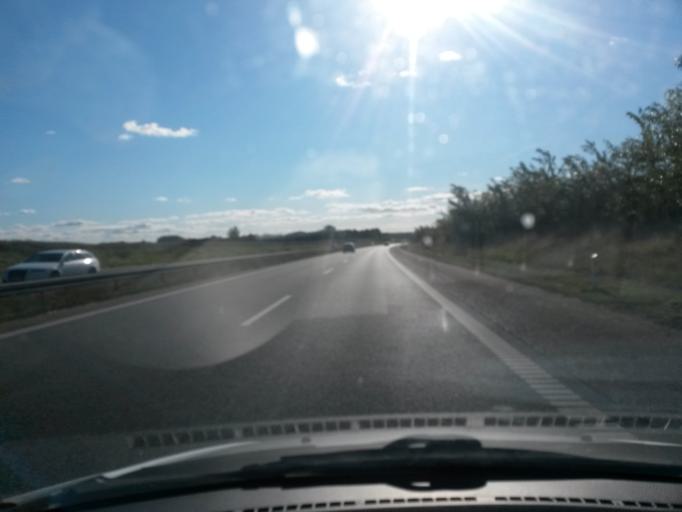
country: DK
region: Central Jutland
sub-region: Arhus Kommune
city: Lystrup
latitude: 56.2284
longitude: 10.2556
